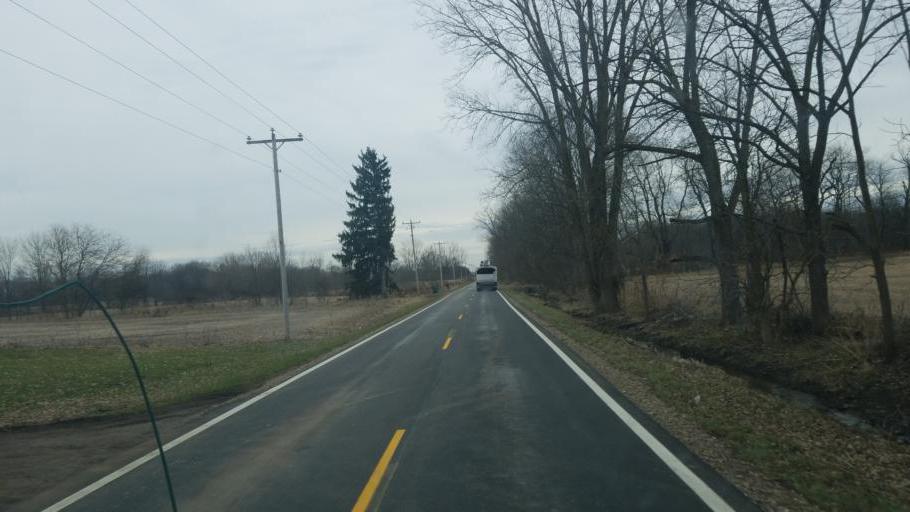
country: US
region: Ohio
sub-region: Licking County
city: Utica
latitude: 40.2593
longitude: -82.5620
